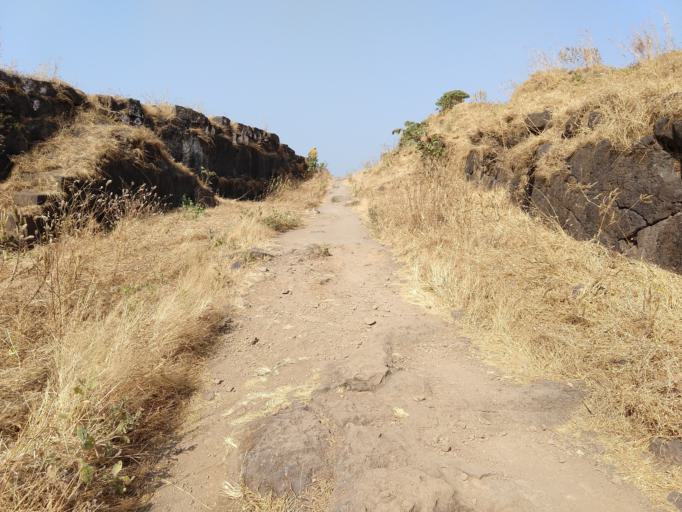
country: IN
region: Maharashtra
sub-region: Pune Division
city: Lonavla
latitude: 18.7138
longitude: 73.4701
